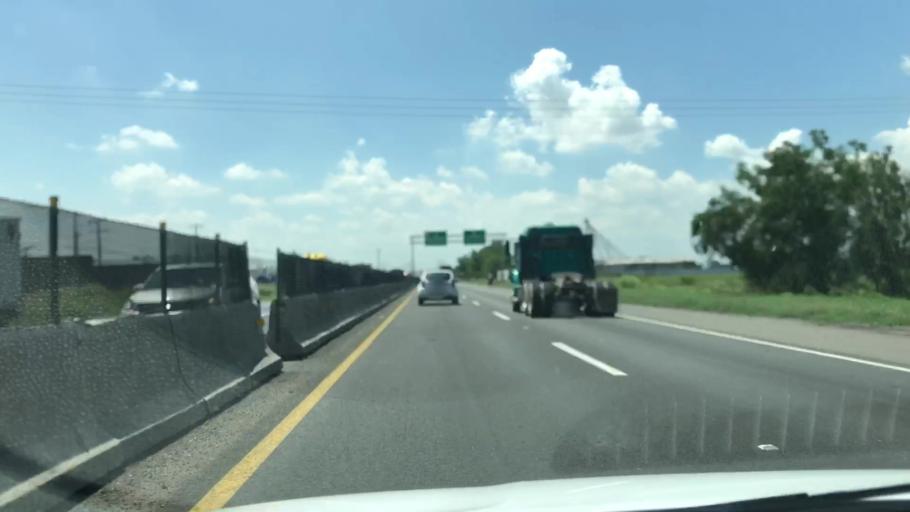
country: MX
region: Guanajuato
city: Valtierrilla
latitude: 20.5416
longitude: -101.1189
